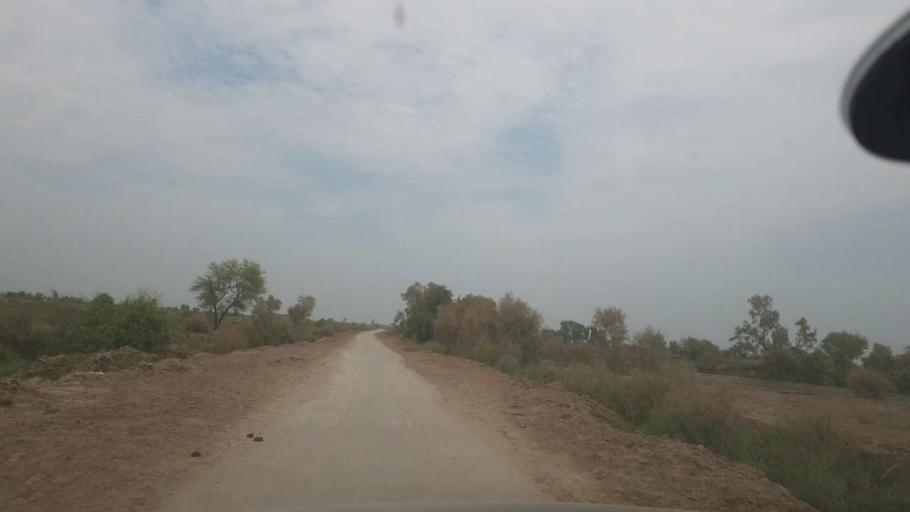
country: PK
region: Balochistan
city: Mehrabpur
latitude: 28.0530
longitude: 68.1441
